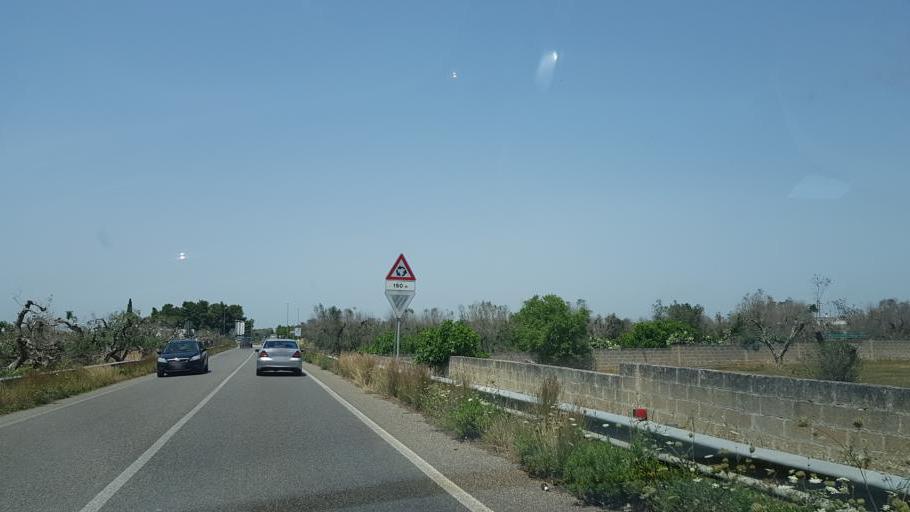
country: IT
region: Apulia
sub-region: Provincia di Lecce
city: Porto Cesareo
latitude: 40.2723
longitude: 17.9030
